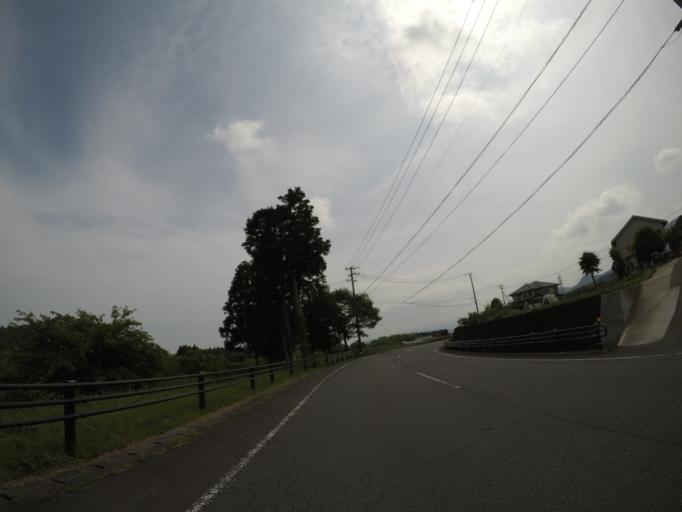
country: JP
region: Shizuoka
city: Fujinomiya
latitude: 35.2998
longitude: 138.5890
